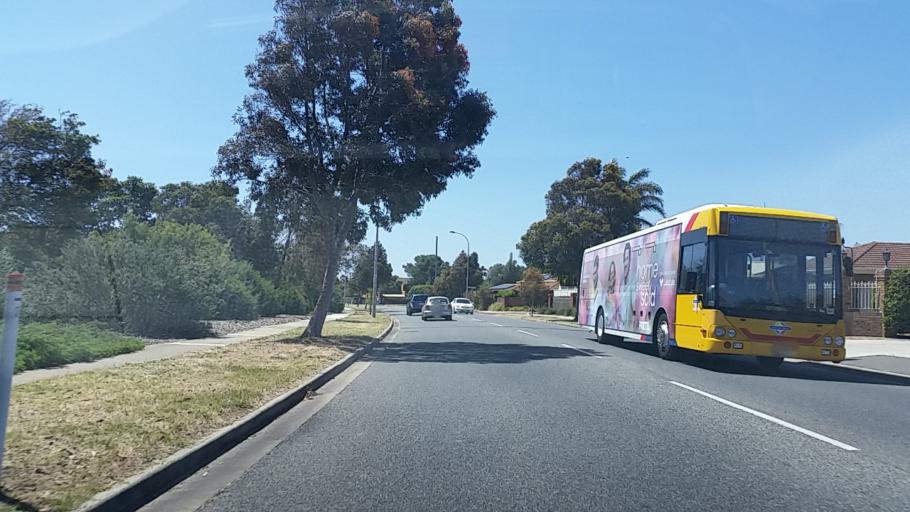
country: AU
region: South Australia
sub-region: Charles Sturt
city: Grange
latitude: -34.8860
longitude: 138.4914
